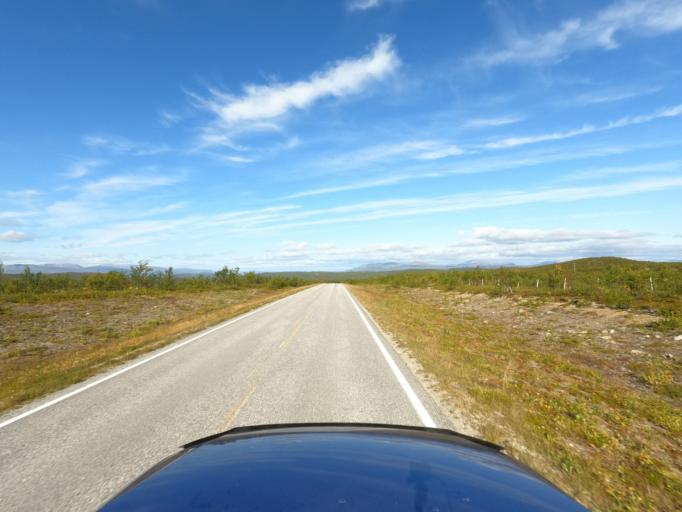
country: NO
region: Finnmark Fylke
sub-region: Karasjok
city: Karasjohka
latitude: 69.7223
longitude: 25.2369
